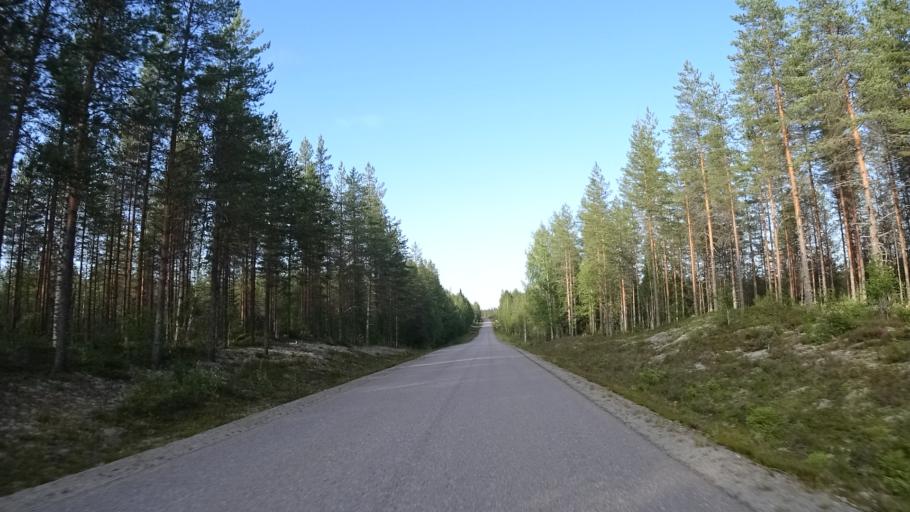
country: FI
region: North Karelia
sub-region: Joensuu
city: Eno
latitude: 63.0619
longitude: 30.5487
